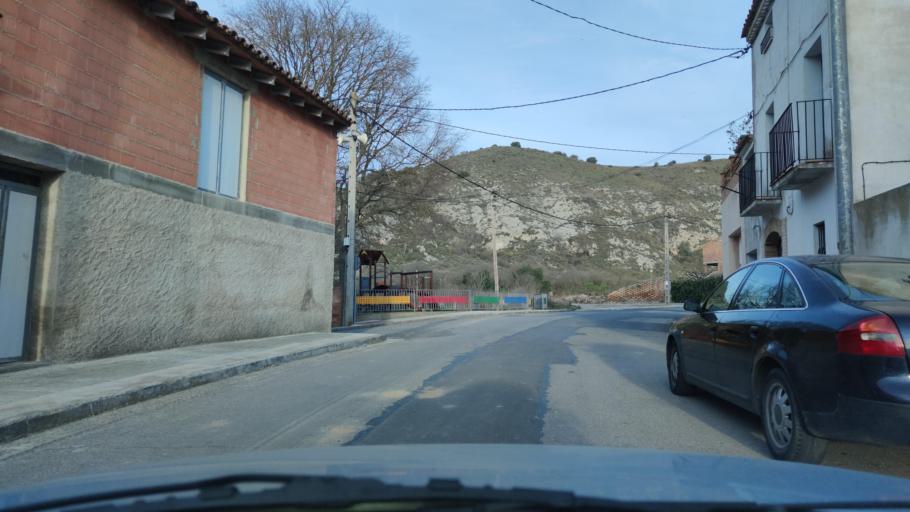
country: ES
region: Catalonia
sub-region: Provincia de Lleida
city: Balaguer
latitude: 41.8229
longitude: 0.8032
